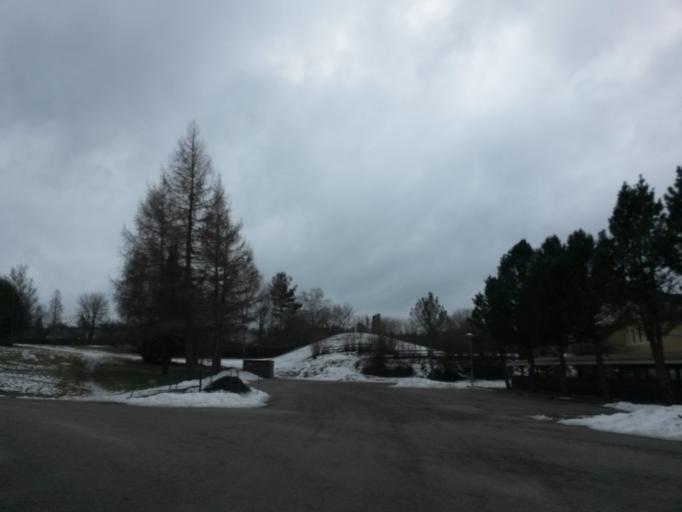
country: SE
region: Vaestra Goetaland
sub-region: Herrljunga Kommun
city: Herrljunga
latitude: 58.0718
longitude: 13.0206
